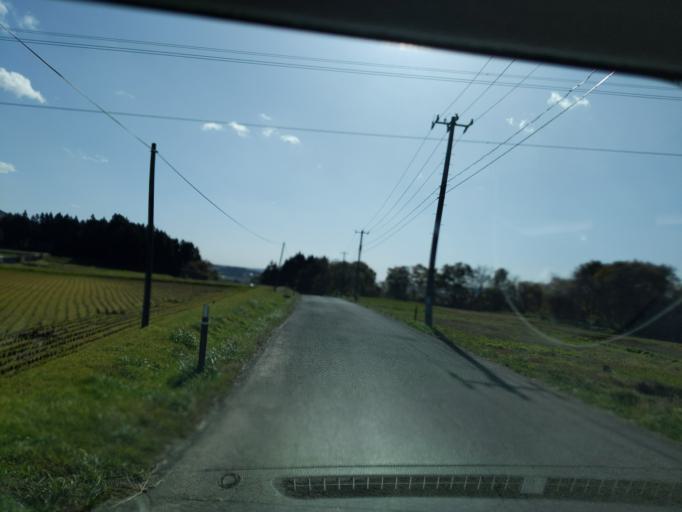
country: JP
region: Iwate
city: Ichinoseki
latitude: 39.0248
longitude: 141.1239
